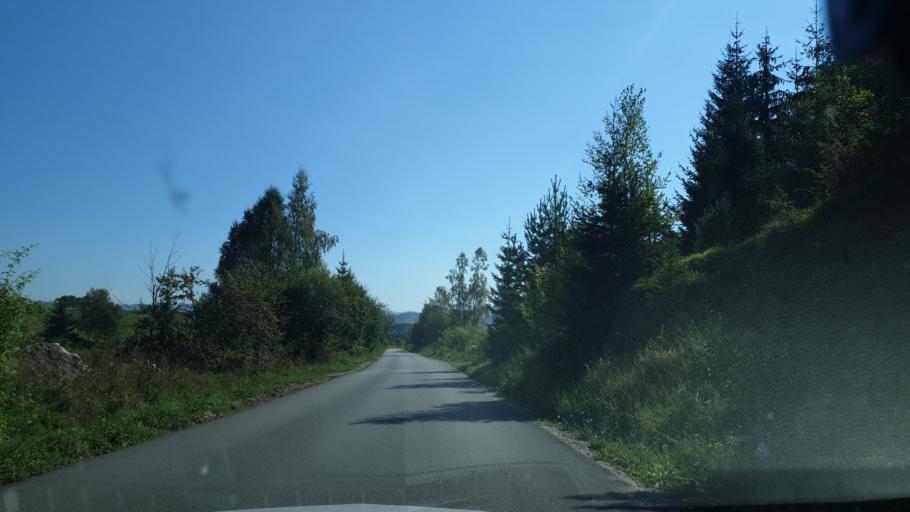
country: RS
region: Central Serbia
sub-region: Zlatiborski Okrug
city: Nova Varos
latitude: 43.4259
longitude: 19.9018
